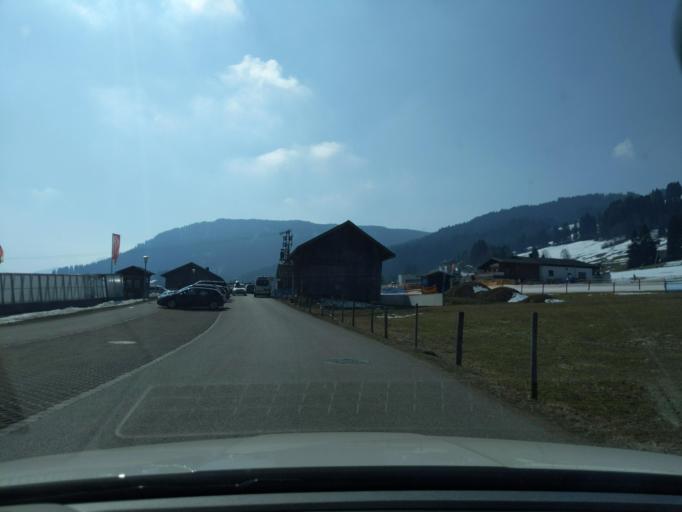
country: DE
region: Bavaria
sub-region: Swabia
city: Obermaiselstein
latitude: 47.4581
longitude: 10.2324
